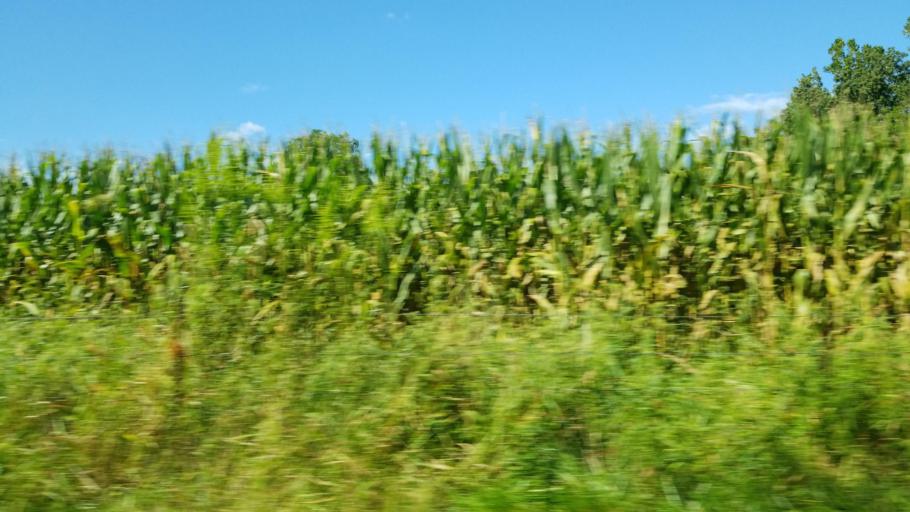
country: US
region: Illinois
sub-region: Williamson County
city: Johnston City
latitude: 37.7844
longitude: -88.8116
